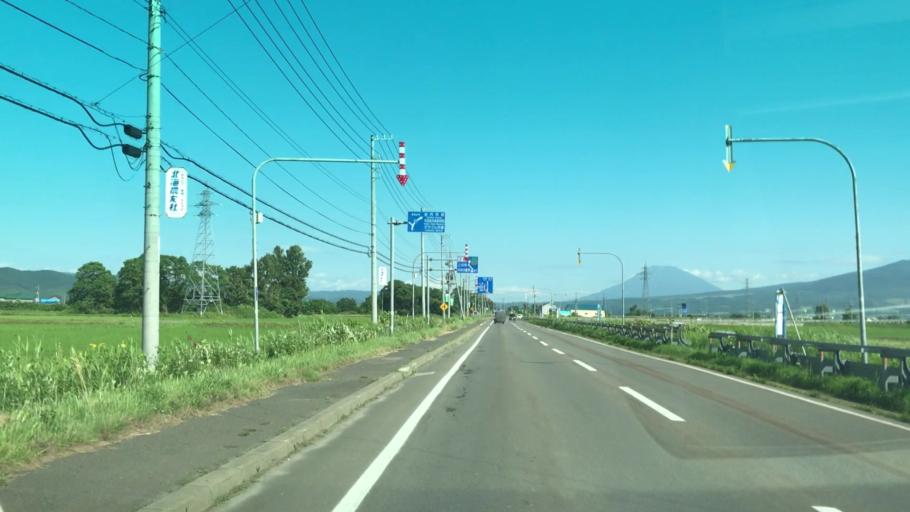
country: JP
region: Hokkaido
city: Iwanai
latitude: 43.0278
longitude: 140.5449
